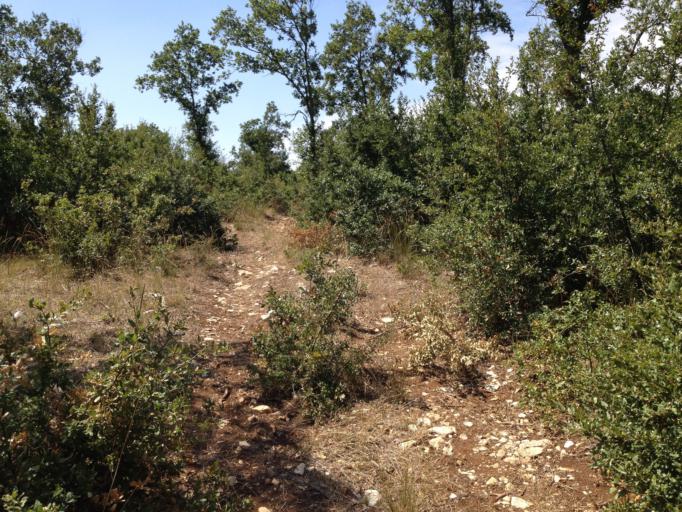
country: IT
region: Apulia
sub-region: Provincia di Bari
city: Gioia del Colle
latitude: 40.8272
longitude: 16.9908
